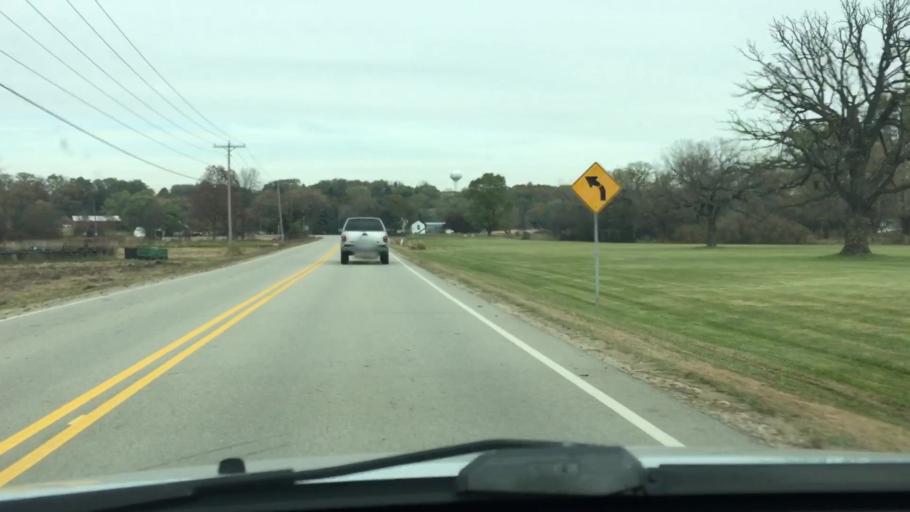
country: US
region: Wisconsin
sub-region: Waukesha County
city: North Prairie
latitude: 42.9173
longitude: -88.4064
